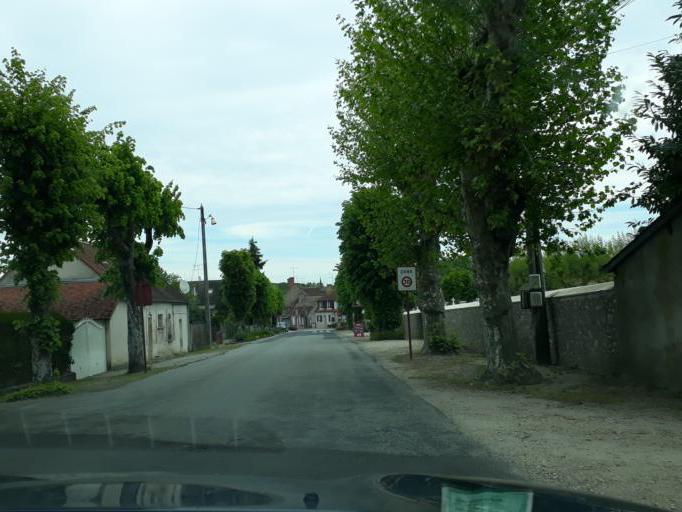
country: FR
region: Centre
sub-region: Departement du Loir-et-Cher
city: Dhuizon
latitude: 47.6516
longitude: 1.6710
